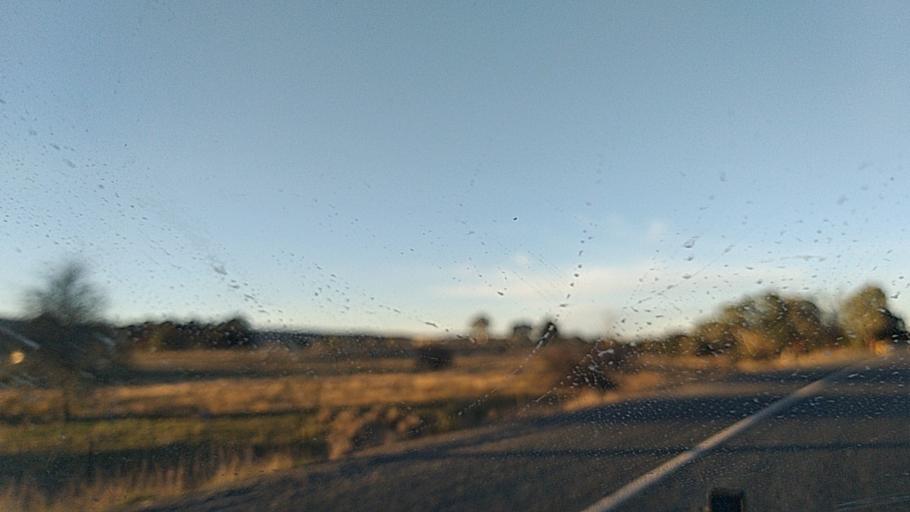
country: AU
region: New South Wales
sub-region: Goulburn Mulwaree
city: Goulburn
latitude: -34.8256
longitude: 149.5980
